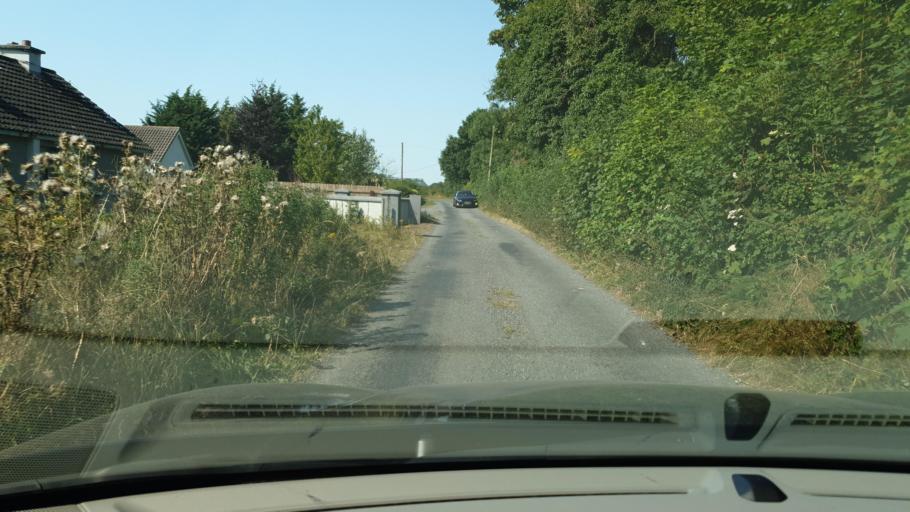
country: IE
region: Leinster
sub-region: An Mhi
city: Athboy
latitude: 53.6069
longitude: -6.9883
